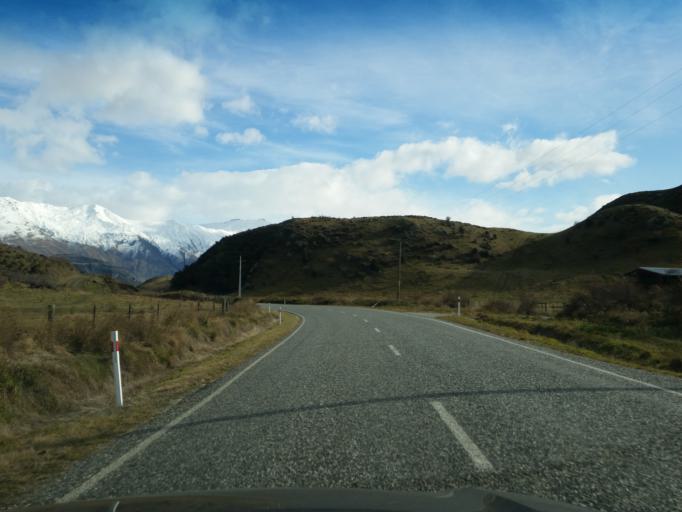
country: NZ
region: Otago
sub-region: Queenstown-Lakes District
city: Wanaka
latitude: -44.6630
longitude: 169.0577
